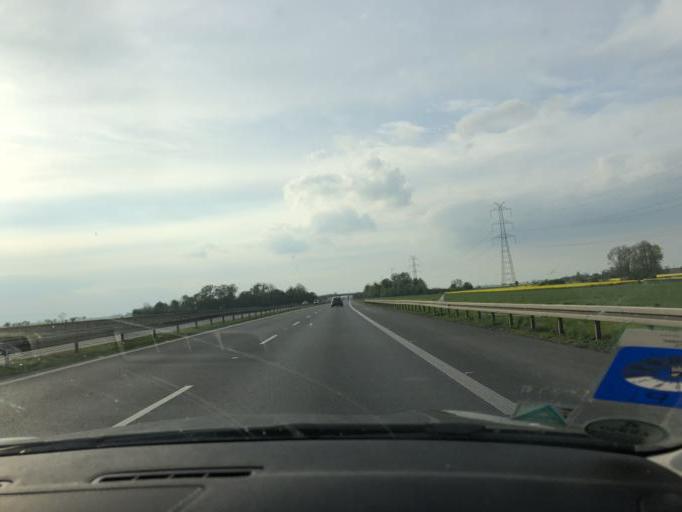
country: PL
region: Lower Silesian Voivodeship
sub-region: Powiat olawski
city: Wierzbno
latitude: 50.9157
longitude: 17.1431
